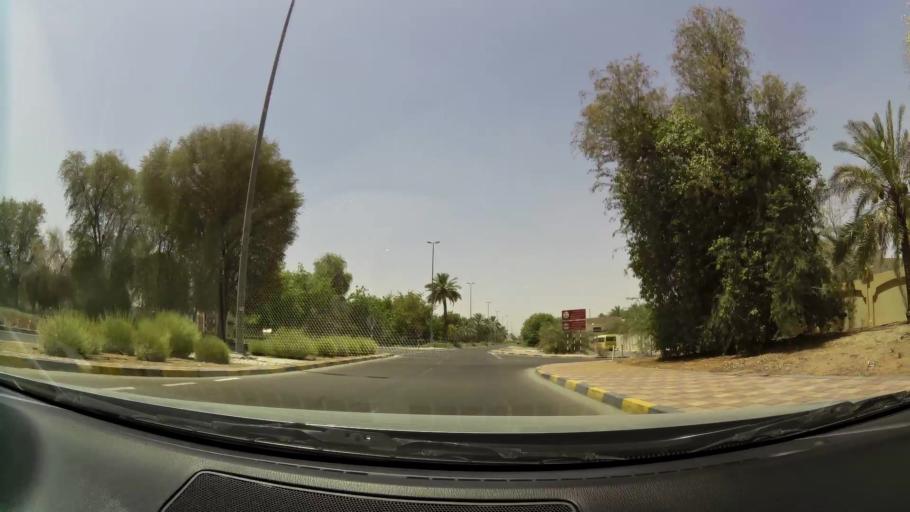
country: OM
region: Al Buraimi
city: Al Buraymi
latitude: 24.2726
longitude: 55.7405
